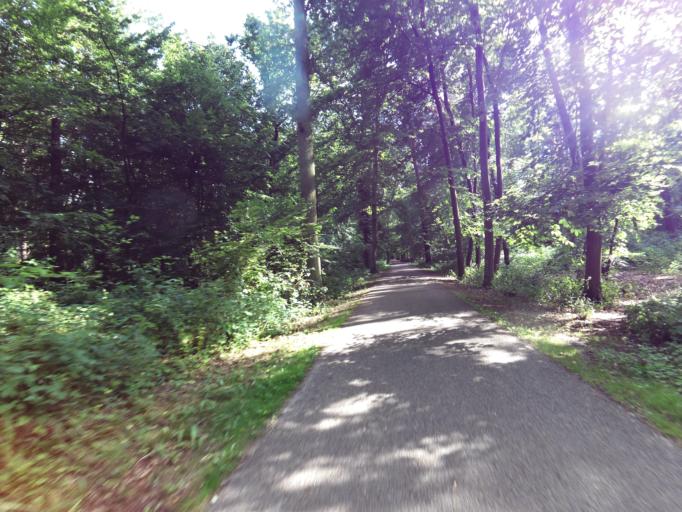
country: NL
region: Limburg
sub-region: Gemeente Brunssum
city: Brunssum
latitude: 50.9498
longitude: 5.9868
